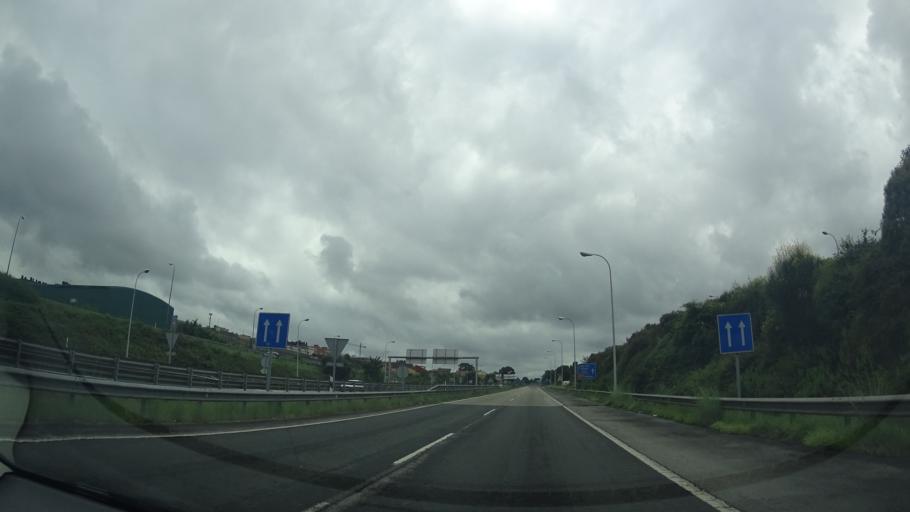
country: ES
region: Asturias
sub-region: Province of Asturias
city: Natahoyo
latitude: 43.5327
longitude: -5.6821
